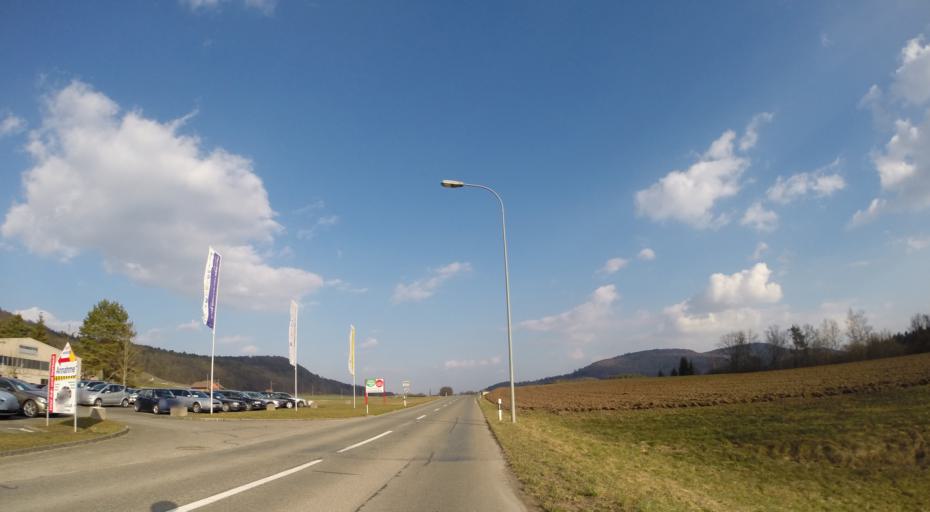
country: CH
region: Thurgau
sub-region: Frauenfeld District
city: Diessenhofen
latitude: 47.6639
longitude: 8.7738
